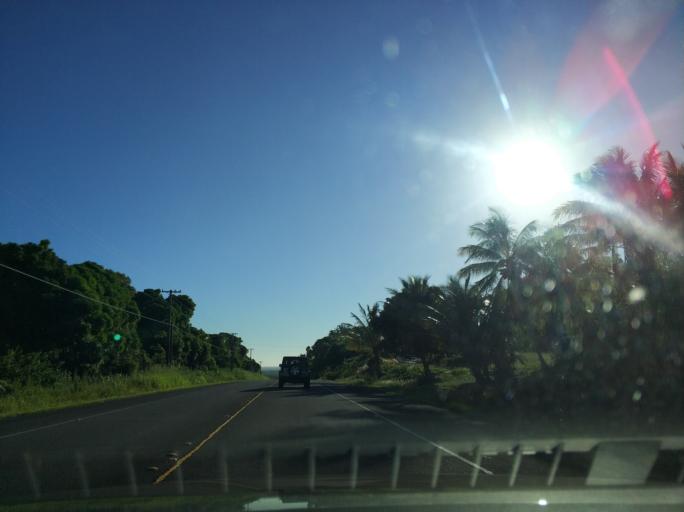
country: US
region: Hawaii
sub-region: Hawaii County
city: Leilani Estates
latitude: 19.3817
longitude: -154.9600
